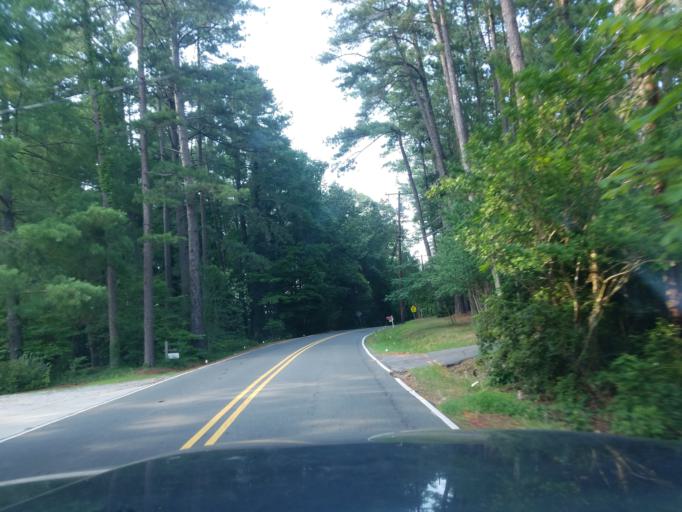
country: US
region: North Carolina
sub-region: Durham County
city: Durham
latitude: 35.9707
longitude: -78.9324
